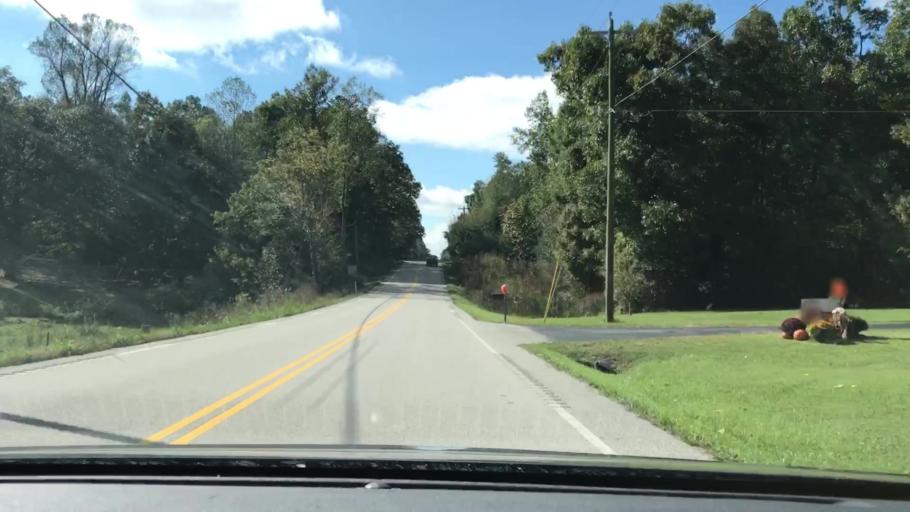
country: US
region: Tennessee
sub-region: Fentress County
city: Jamestown
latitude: 36.3819
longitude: -84.8986
